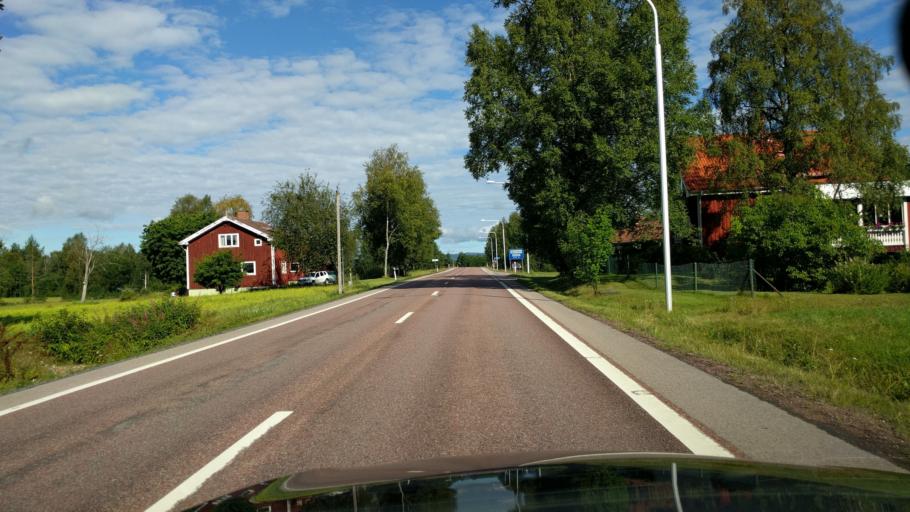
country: SE
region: Dalarna
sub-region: Alvdalens Kommun
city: AElvdalen
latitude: 61.2107
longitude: 14.0573
